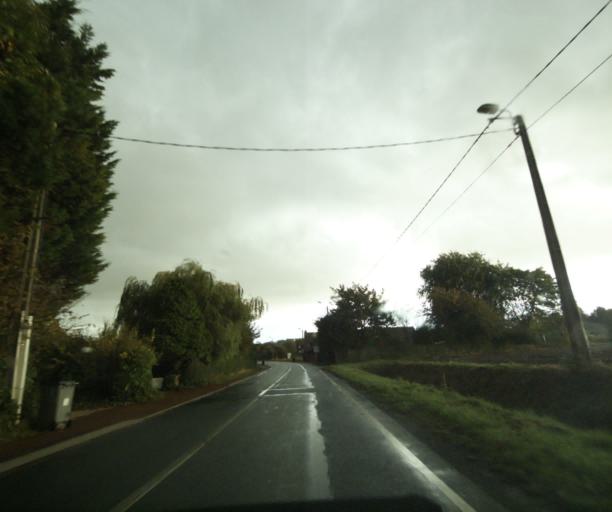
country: FR
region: Nord-Pas-de-Calais
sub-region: Departement du Nord
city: Roncq
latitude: 50.7421
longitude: 3.1126
